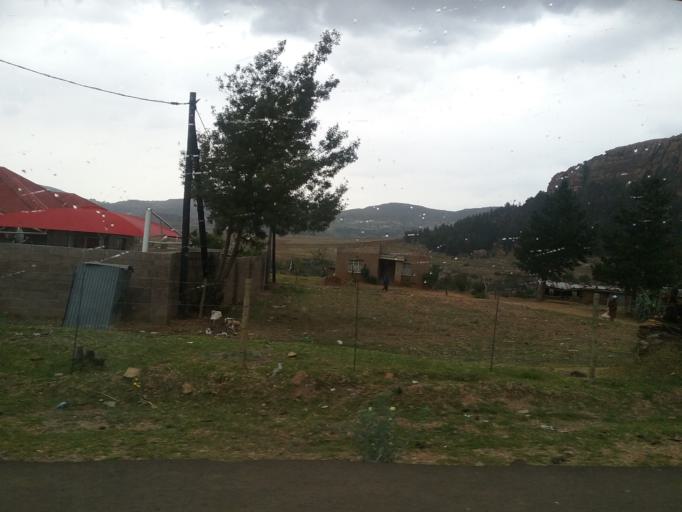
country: LS
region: Maseru
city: Nako
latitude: -29.4684
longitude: 27.7365
